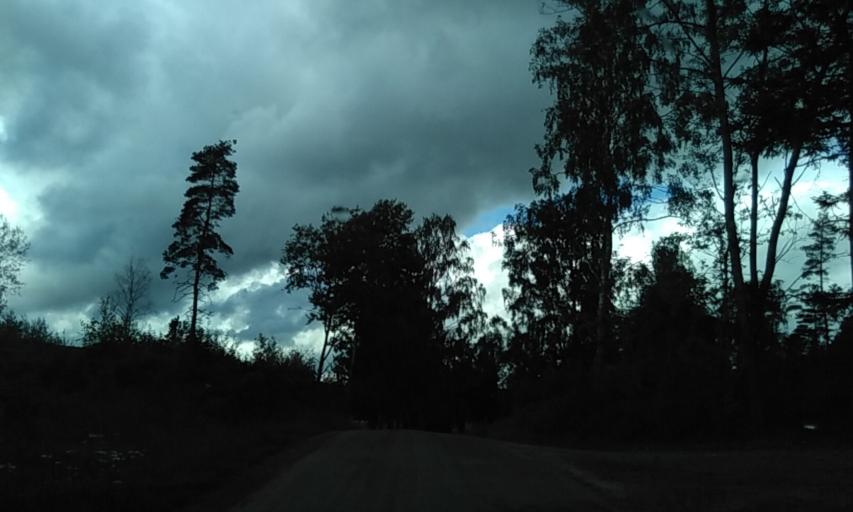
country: SE
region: Vaestra Goetaland
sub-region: Vargarda Kommun
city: Jonstorp
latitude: 57.9952
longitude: 12.6379
